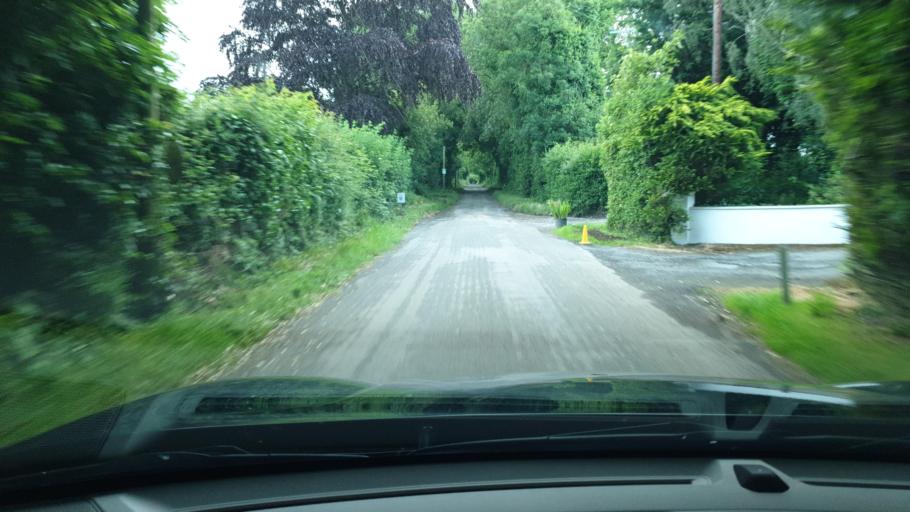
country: IE
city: Kentstown
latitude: 53.5781
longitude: -6.5238
